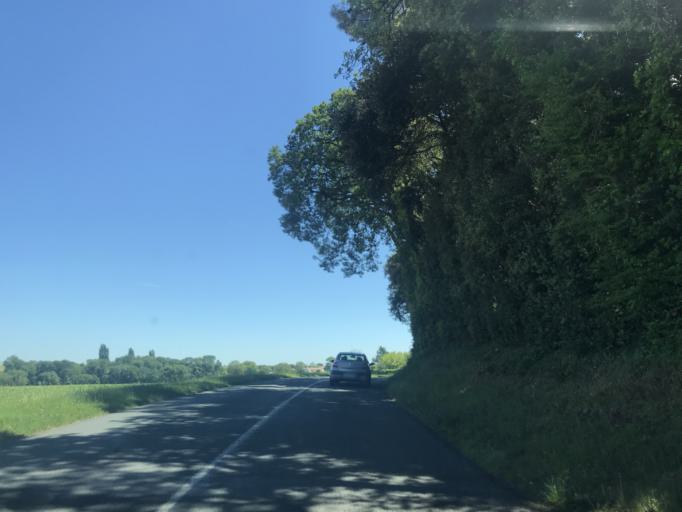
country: FR
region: Poitou-Charentes
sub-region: Departement de la Charente-Maritime
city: Meschers-sur-Gironde
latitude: 45.5902
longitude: -0.9640
